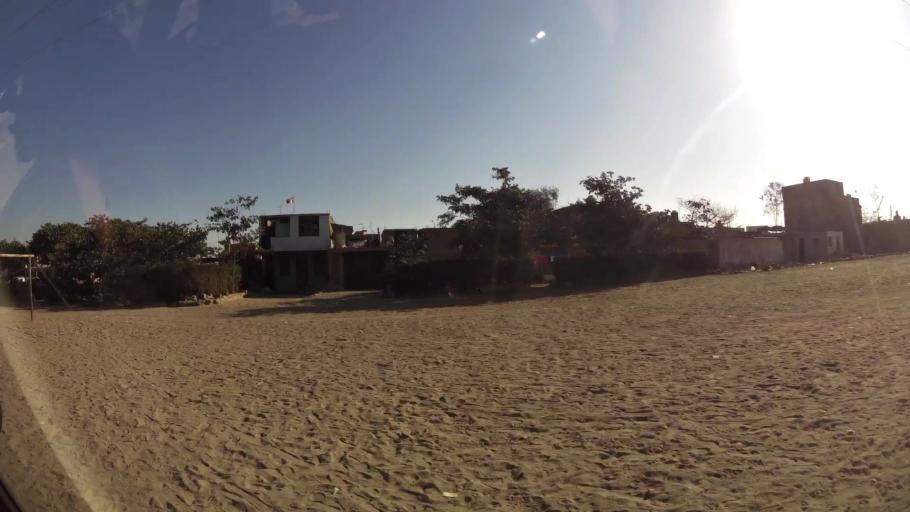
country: PE
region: Ica
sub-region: Provincia de Ica
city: La Tinguina
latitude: -14.0520
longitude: -75.6933
